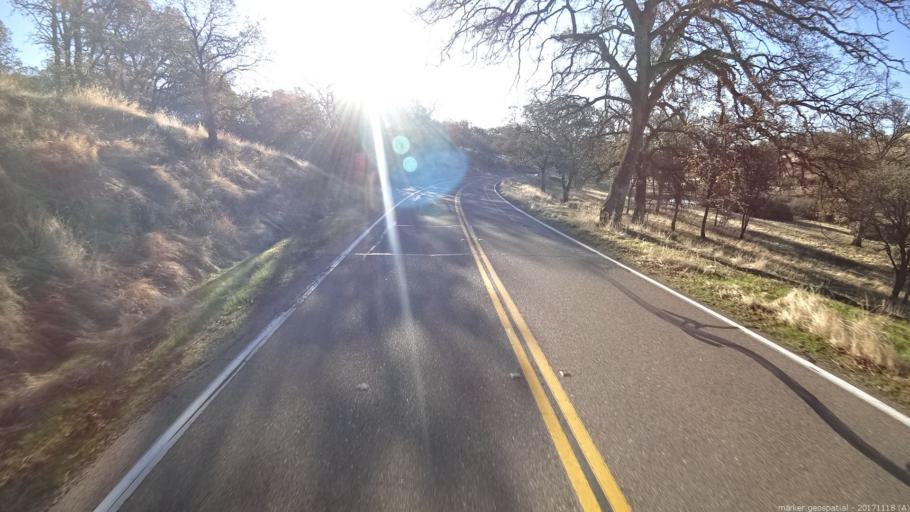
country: US
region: California
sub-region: Shasta County
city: Cottonwood
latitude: 40.4134
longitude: -122.2829
